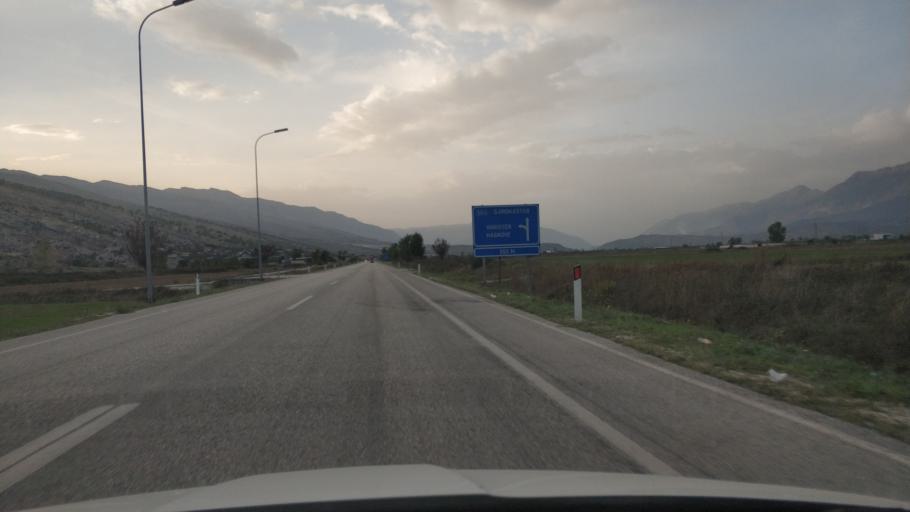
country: AL
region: Gjirokaster
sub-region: Rrethi i Gjirokastres
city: Dervician
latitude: 40.0086
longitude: 20.2057
